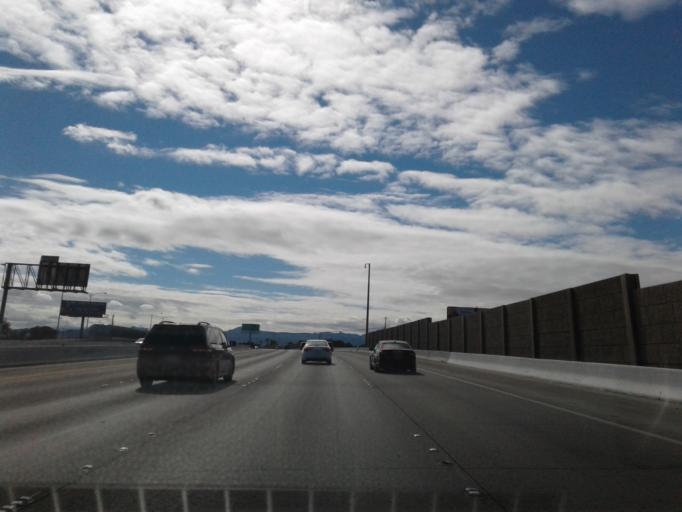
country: US
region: Nevada
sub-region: Clark County
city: Winchester
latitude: 36.1314
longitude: -115.0897
